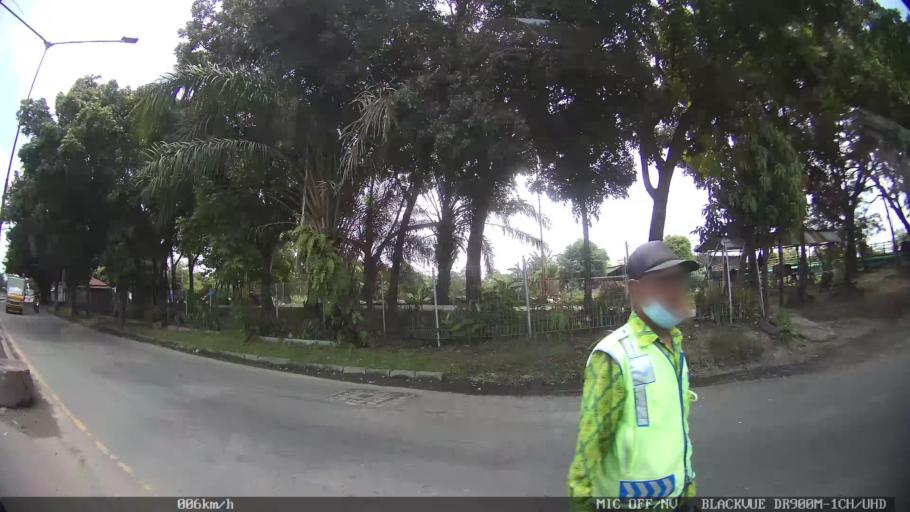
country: ID
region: North Sumatra
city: Labuhan Deli
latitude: 3.7077
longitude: 98.6797
